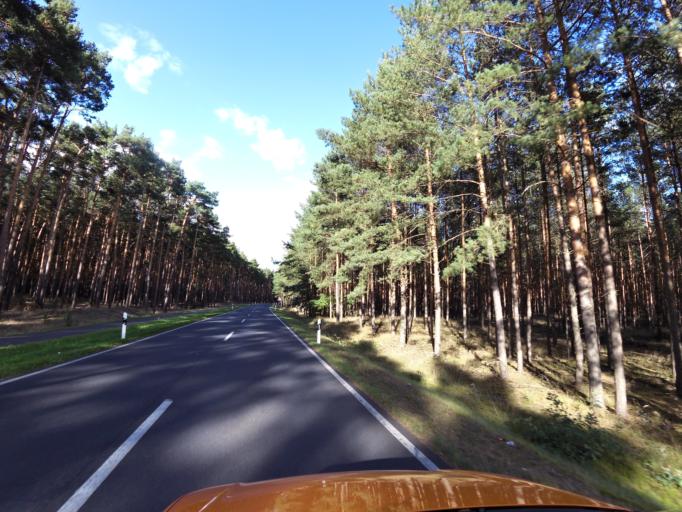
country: DE
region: Brandenburg
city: Luckenwalde
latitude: 52.1341
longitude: 13.1734
